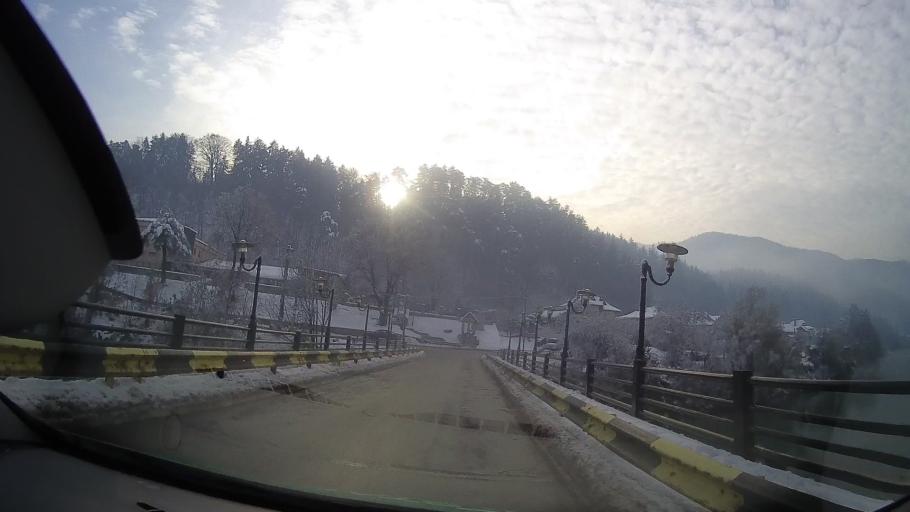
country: RO
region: Neamt
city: Piatra Neamt
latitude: 46.9241
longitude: 26.3647
